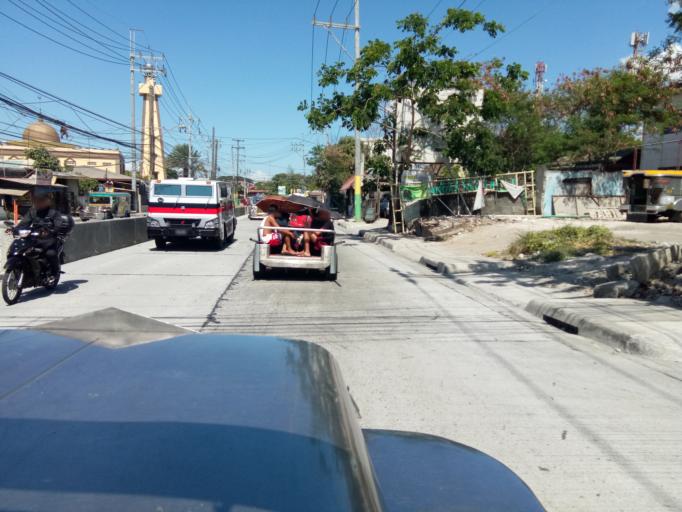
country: PH
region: Calabarzon
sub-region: Province of Cavite
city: Dasmarinas
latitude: 14.3505
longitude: 120.9412
